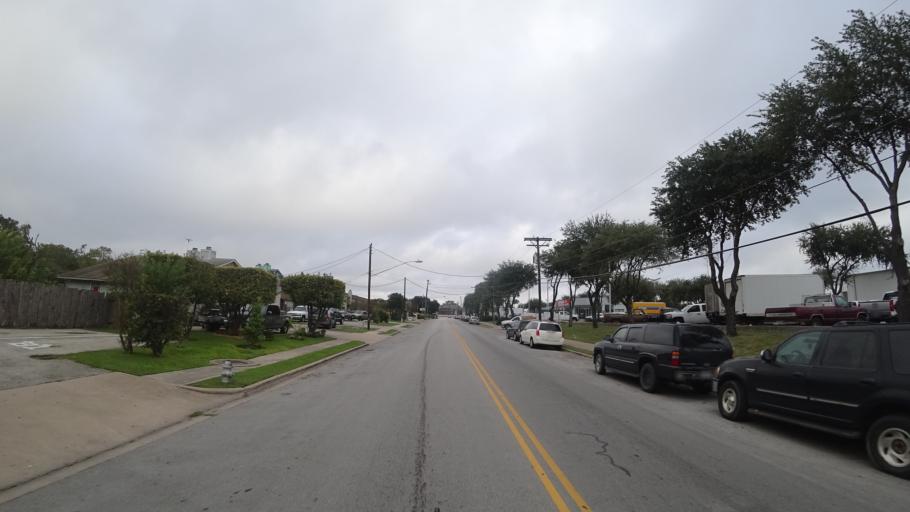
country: US
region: Texas
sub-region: Travis County
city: Wells Branch
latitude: 30.3498
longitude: -97.6899
